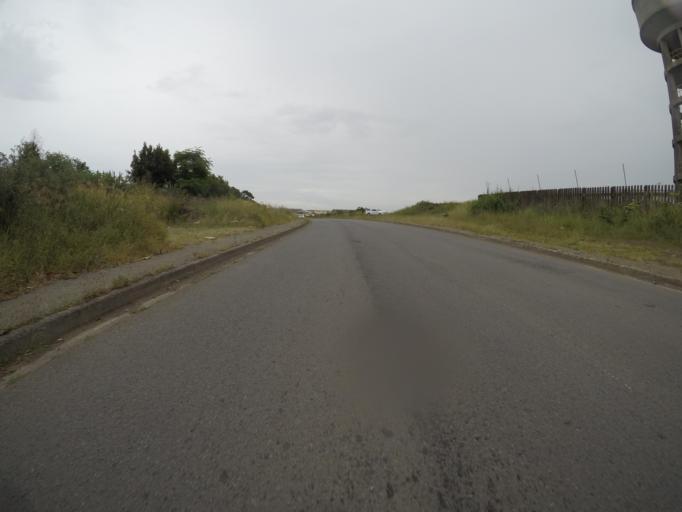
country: ZA
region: Eastern Cape
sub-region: Buffalo City Metropolitan Municipality
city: East London
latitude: -32.9677
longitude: 27.8288
